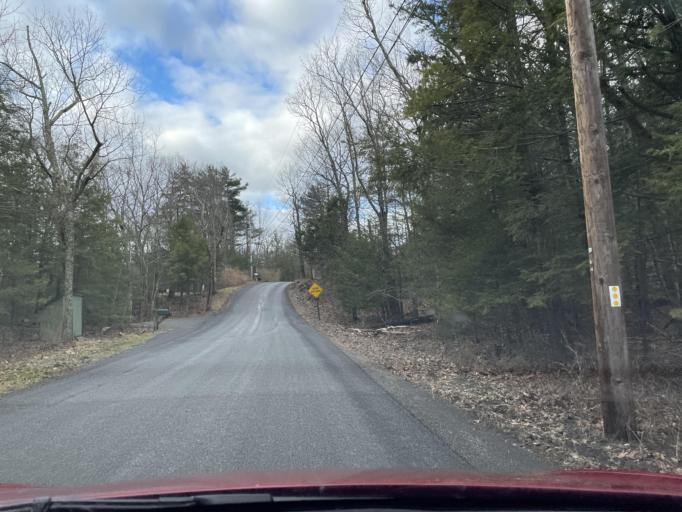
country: US
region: New York
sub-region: Ulster County
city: Zena
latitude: 42.0741
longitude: -74.0651
